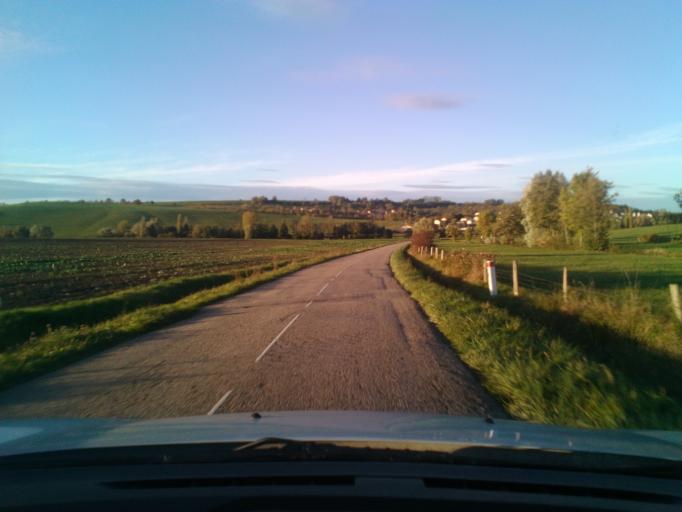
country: FR
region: Lorraine
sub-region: Departement des Vosges
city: Charmes
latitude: 48.3558
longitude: 6.2552
